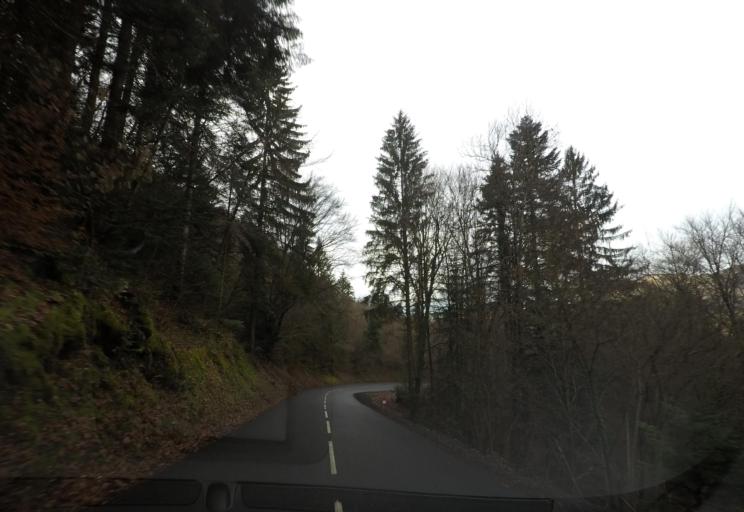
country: FR
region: Rhone-Alpes
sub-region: Departement de la Haute-Savoie
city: Ayse
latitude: 46.0605
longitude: 6.4367
